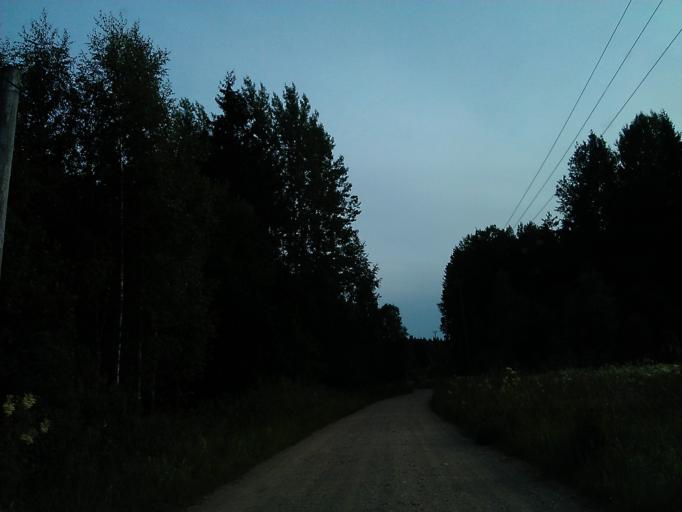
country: LV
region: Amatas Novads
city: Drabesi
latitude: 57.2007
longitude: 25.1673
